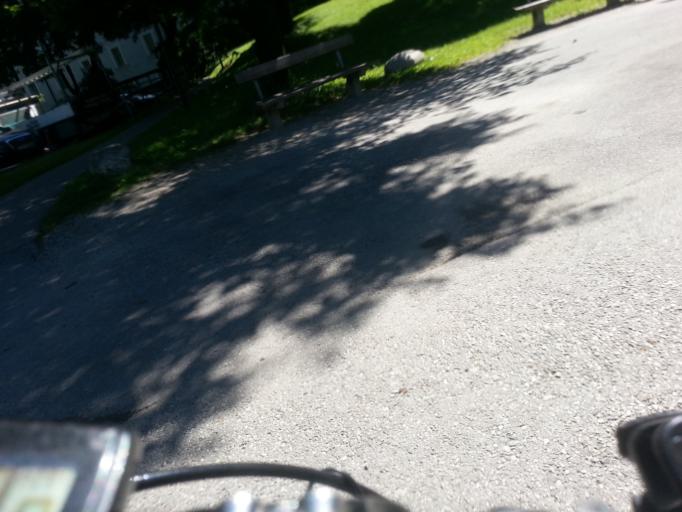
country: AT
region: Salzburg
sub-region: Salzburg Stadt
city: Salzburg
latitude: 47.8027
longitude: 13.0387
